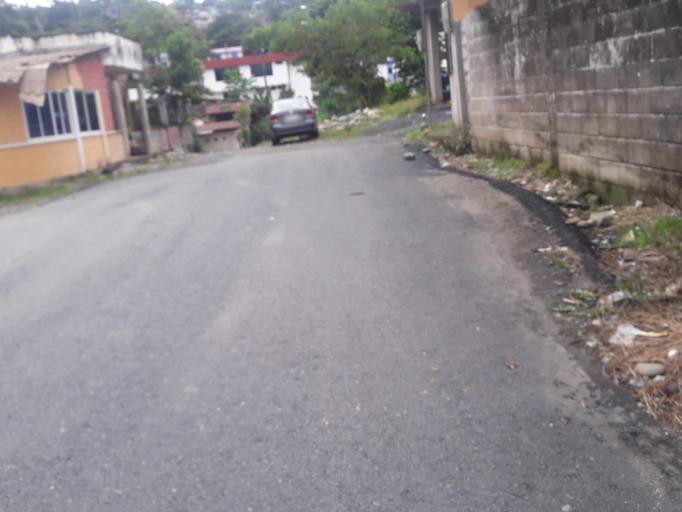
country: EC
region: Napo
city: Tena
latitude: -0.9957
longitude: -77.8098
